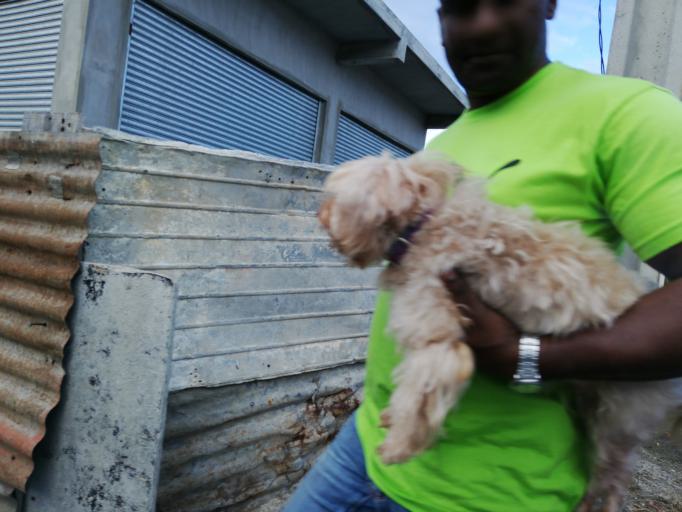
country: MU
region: Plaines Wilhems
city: Ebene
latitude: -20.2335
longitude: 57.4594
